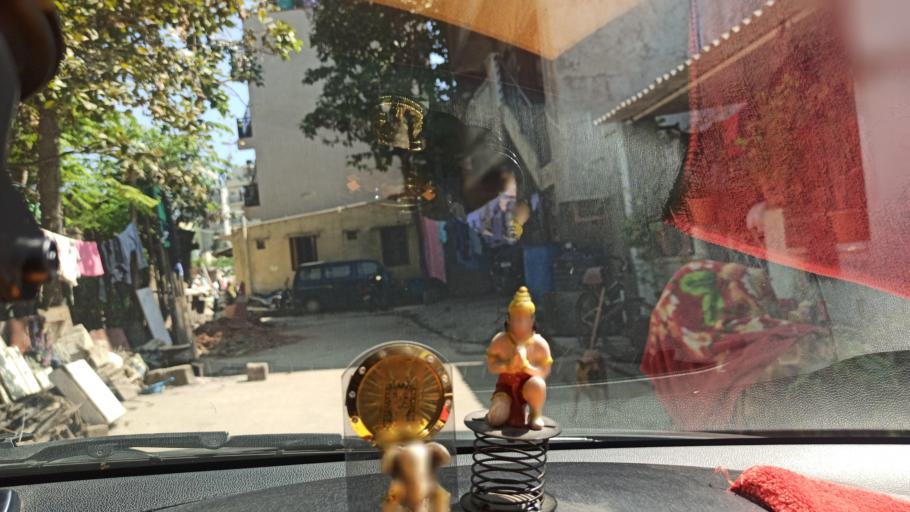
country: IN
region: Karnataka
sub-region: Bangalore Urban
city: Bangalore
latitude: 12.9581
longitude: 77.6953
